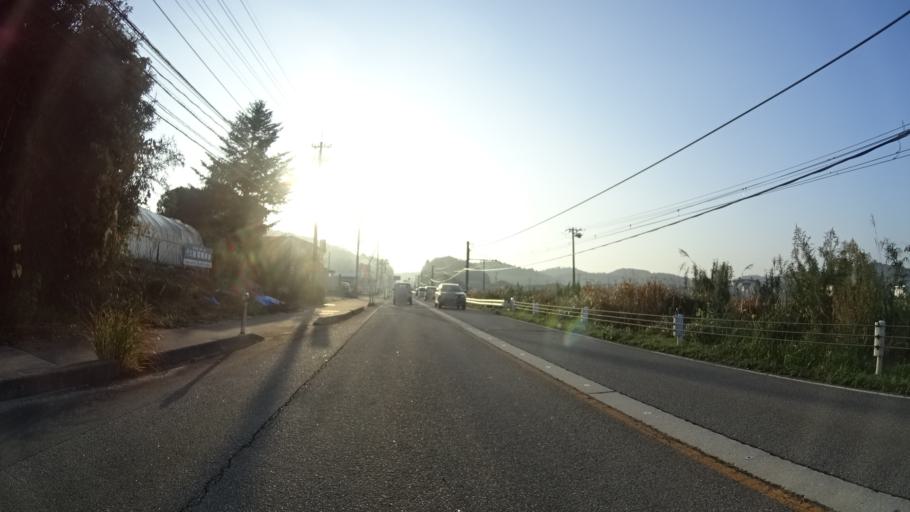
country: JP
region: Ishikawa
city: Nanao
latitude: 37.0619
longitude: 136.9424
